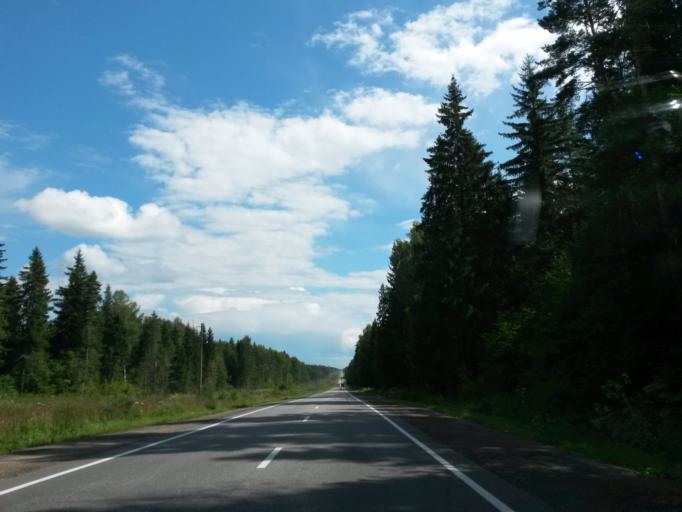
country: RU
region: Jaroslavl
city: Gavrilov-Yam
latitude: 57.2684
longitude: 39.9774
